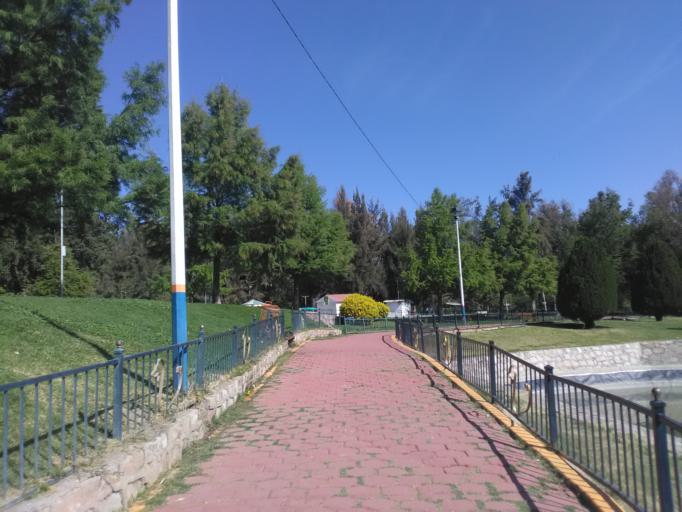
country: MX
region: Durango
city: Victoria de Durango
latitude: 24.0244
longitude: -104.6865
